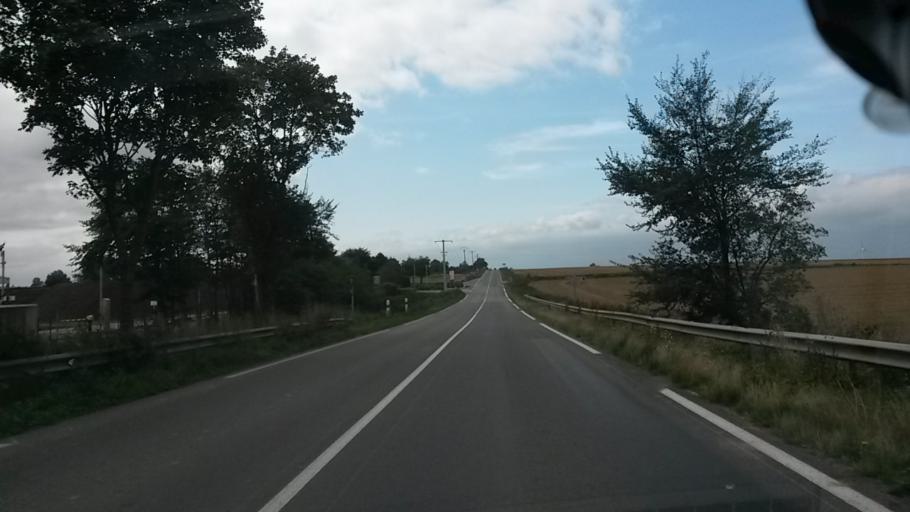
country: FR
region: Nord-Pas-de-Calais
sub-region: Departement du Pas-de-Calais
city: Hermies
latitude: 50.1480
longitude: 3.0708
